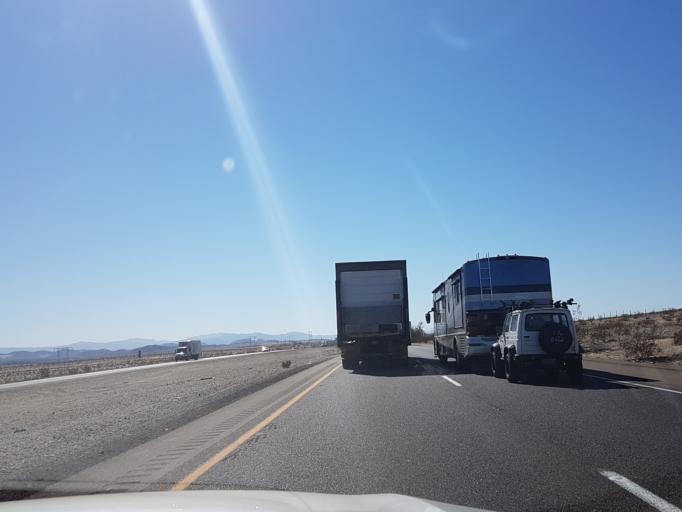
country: US
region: California
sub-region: San Bernardino County
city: Fort Irwin
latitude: 35.0416
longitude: -116.4575
